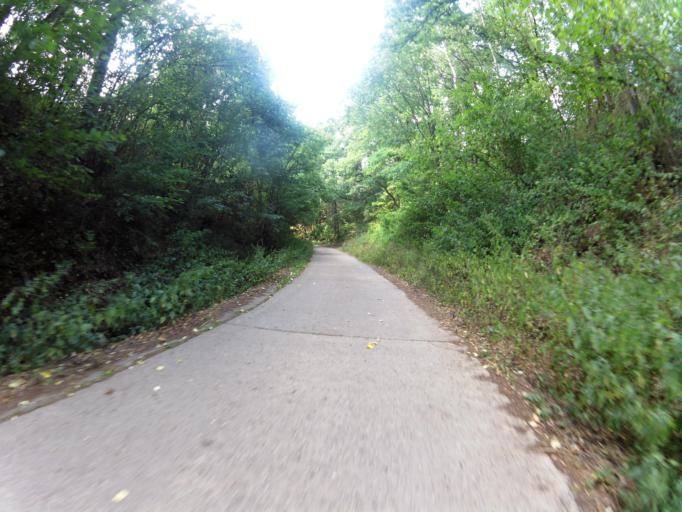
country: DE
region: Bavaria
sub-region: Regierungsbezirk Unterfranken
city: Ochsenfurt
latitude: 49.6540
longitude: 10.0592
